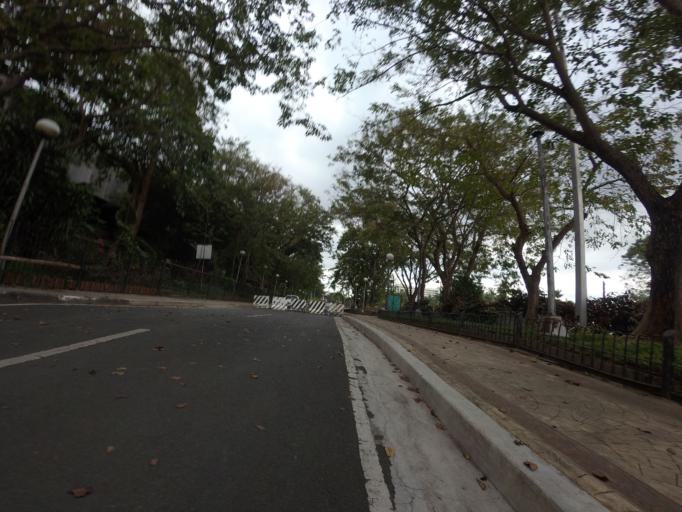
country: PH
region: Metro Manila
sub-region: City of Manila
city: Port Area
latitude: 14.5568
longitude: 120.9802
